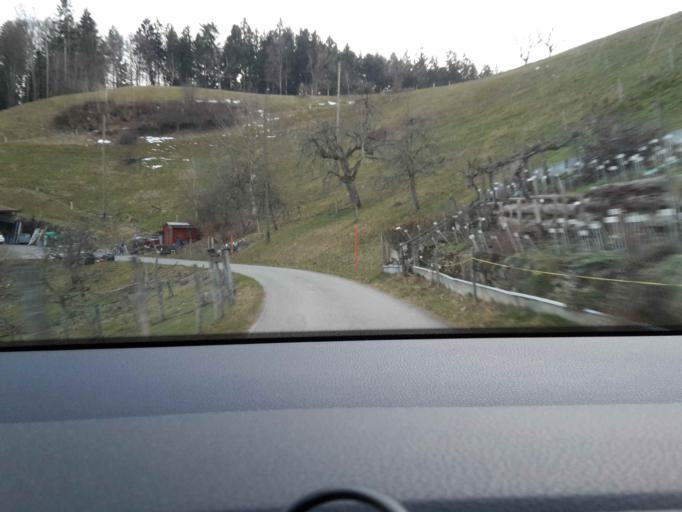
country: CH
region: Bern
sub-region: Oberaargau
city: Rohrbach
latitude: 47.1272
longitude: 7.7947
